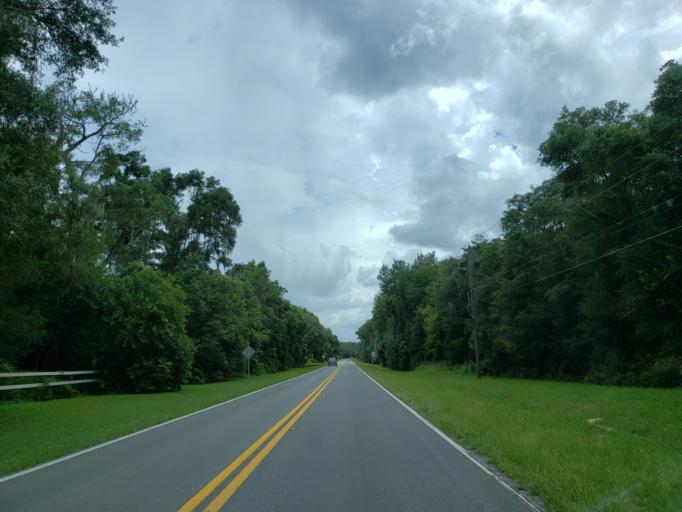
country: US
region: Florida
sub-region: Citrus County
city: Floral City
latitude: 28.6465
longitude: -82.2645
